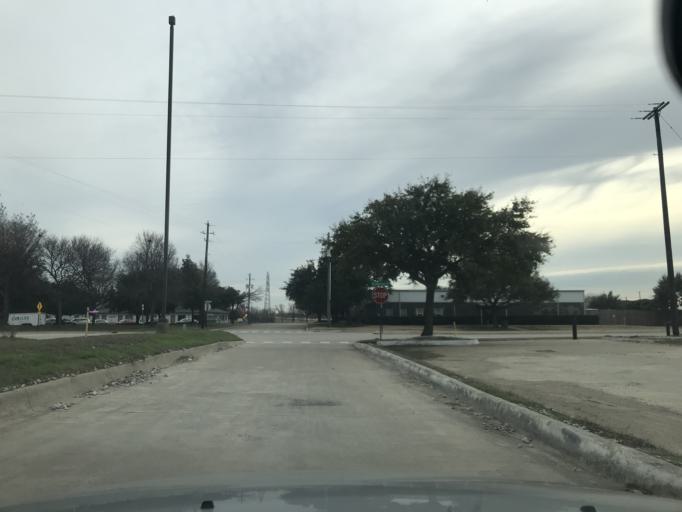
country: US
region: Texas
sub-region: Dallas County
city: Carrollton
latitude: 32.9805
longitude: -96.9228
